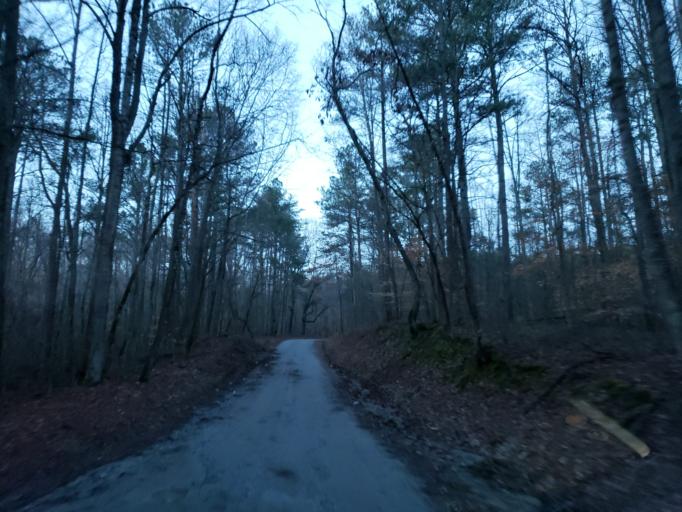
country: US
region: Georgia
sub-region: Cherokee County
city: Ball Ground
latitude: 34.2908
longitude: -84.3014
